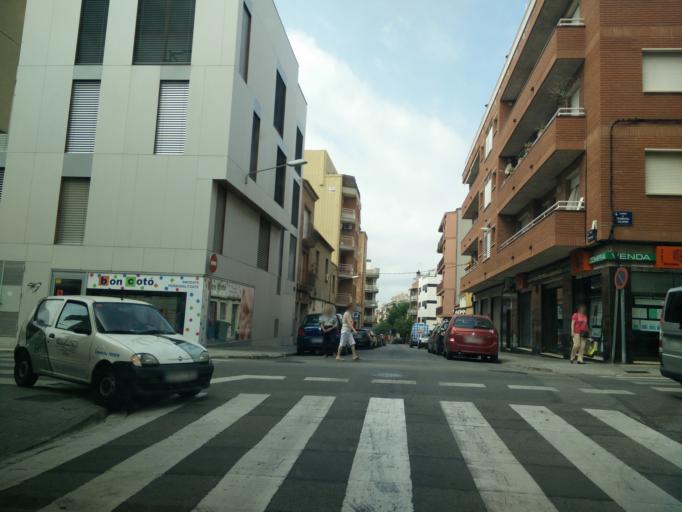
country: ES
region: Catalonia
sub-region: Provincia de Barcelona
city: Terrassa
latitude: 41.5731
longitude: 2.0135
